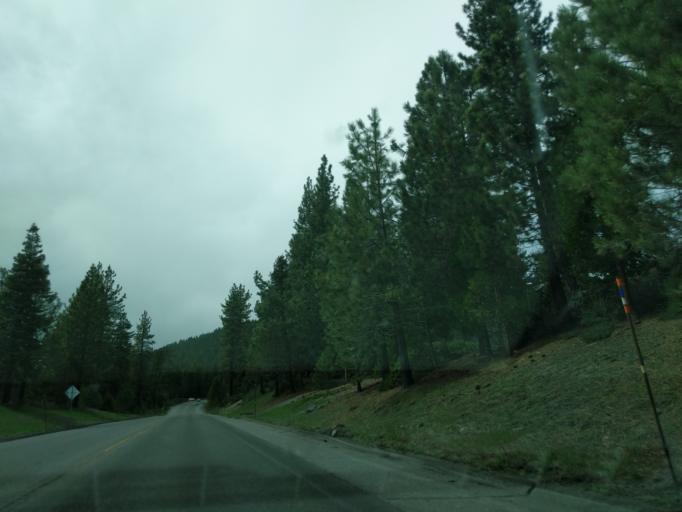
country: US
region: California
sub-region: Placer County
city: Tahoe Vista
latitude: 39.2532
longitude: -120.0389
